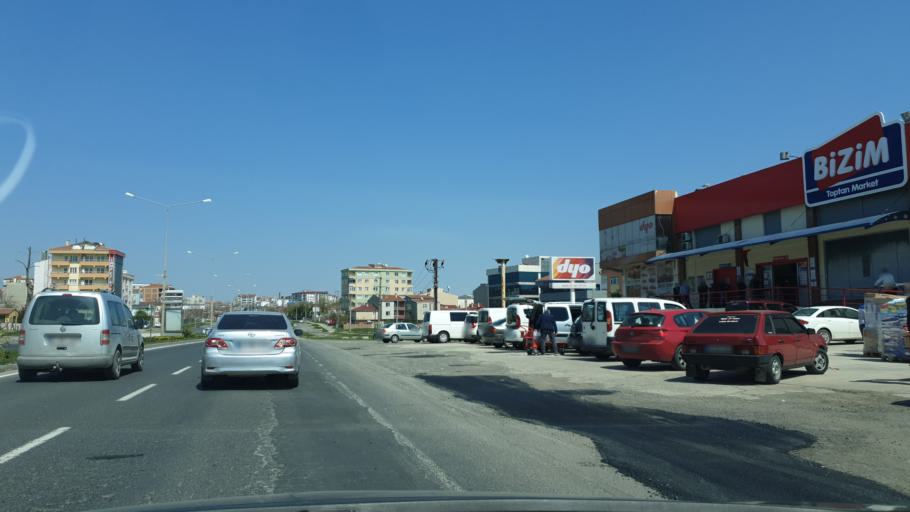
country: TR
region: Tekirdag
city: Corlu
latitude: 41.1567
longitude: 27.7832
